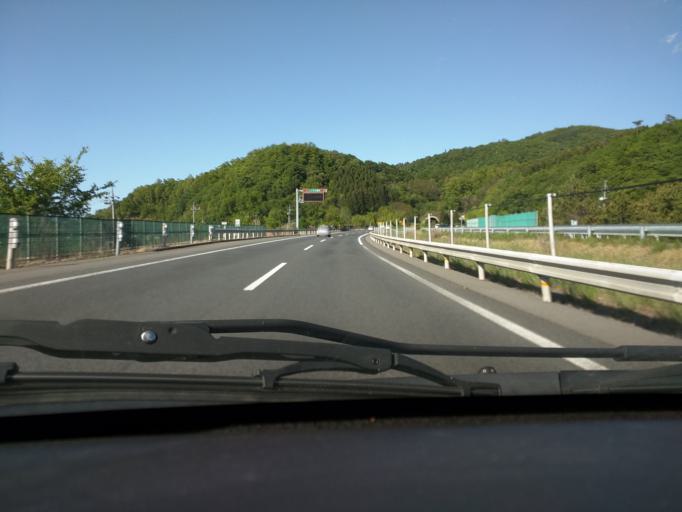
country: JP
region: Nagano
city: Nagano-shi
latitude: 36.5909
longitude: 138.2184
